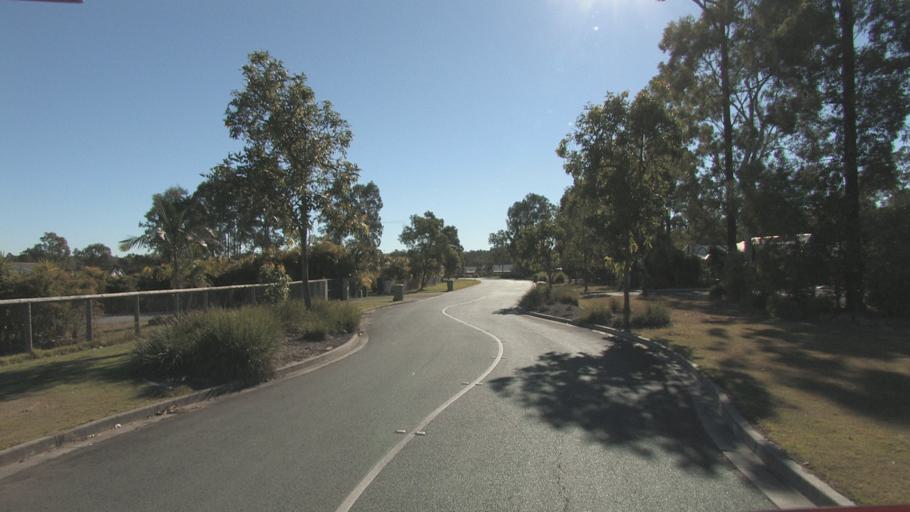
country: AU
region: Queensland
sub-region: Logan
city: North Maclean
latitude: -27.7577
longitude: 152.9666
